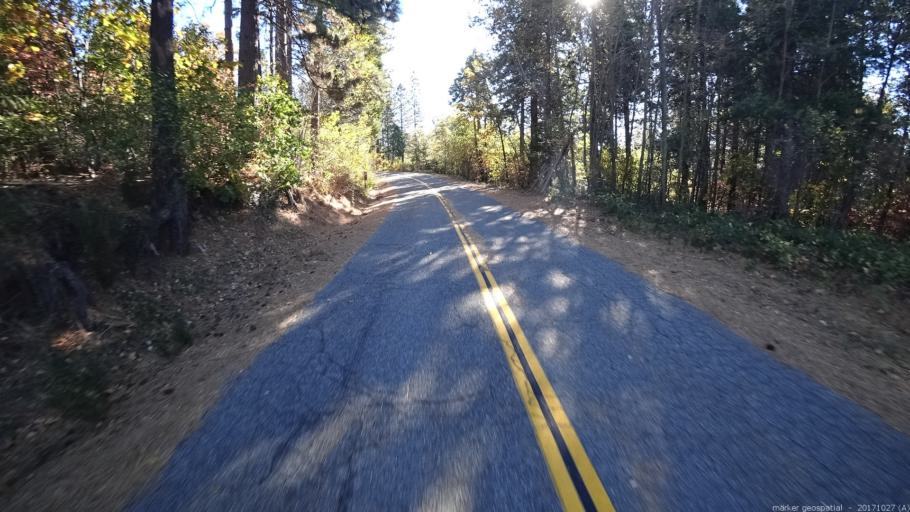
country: US
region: California
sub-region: Shasta County
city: Burney
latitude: 40.8619
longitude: -121.9147
